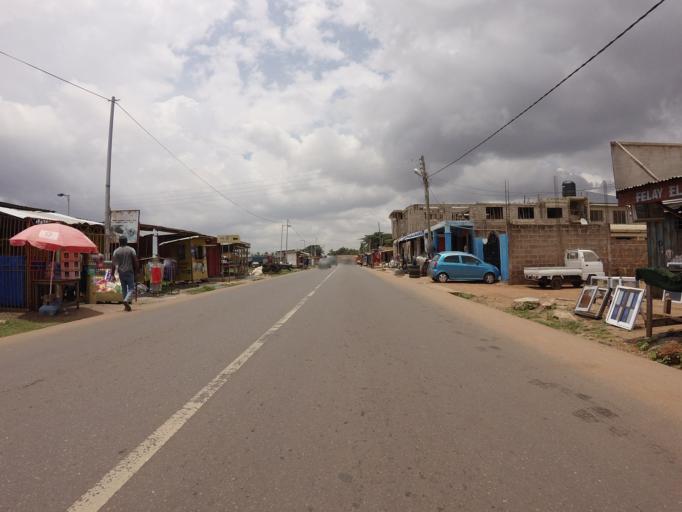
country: GH
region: Greater Accra
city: Medina Estates
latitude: 5.6791
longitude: -0.1498
